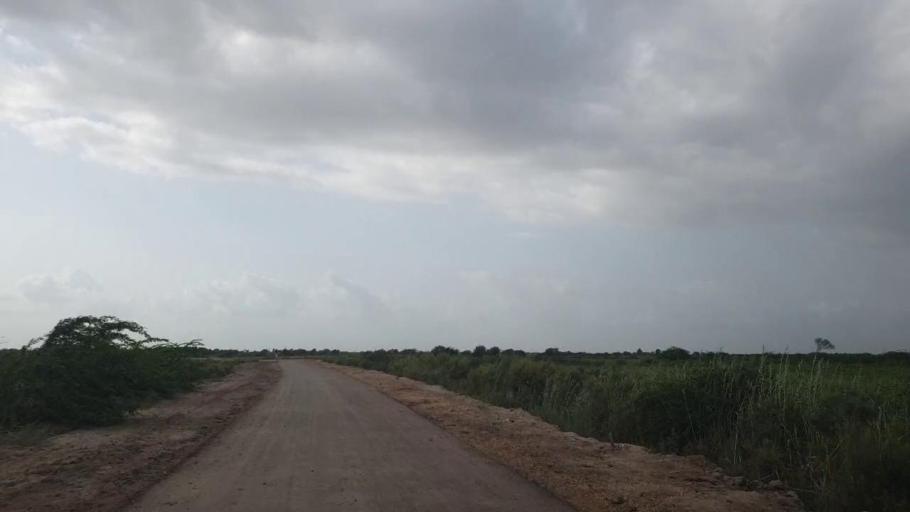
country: PK
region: Sindh
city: Kadhan
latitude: 24.5805
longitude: 69.0583
